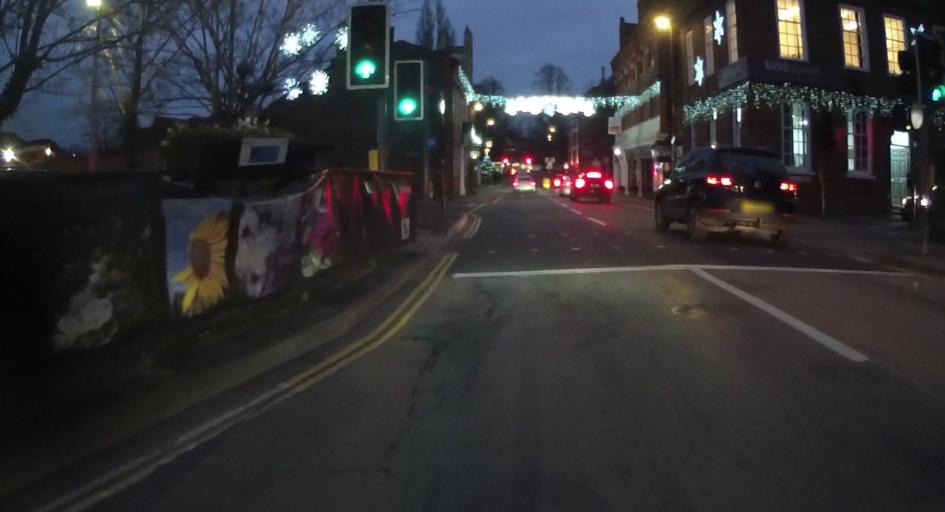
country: GB
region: England
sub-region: Surrey
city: Farnham
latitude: 51.2146
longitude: -0.7961
